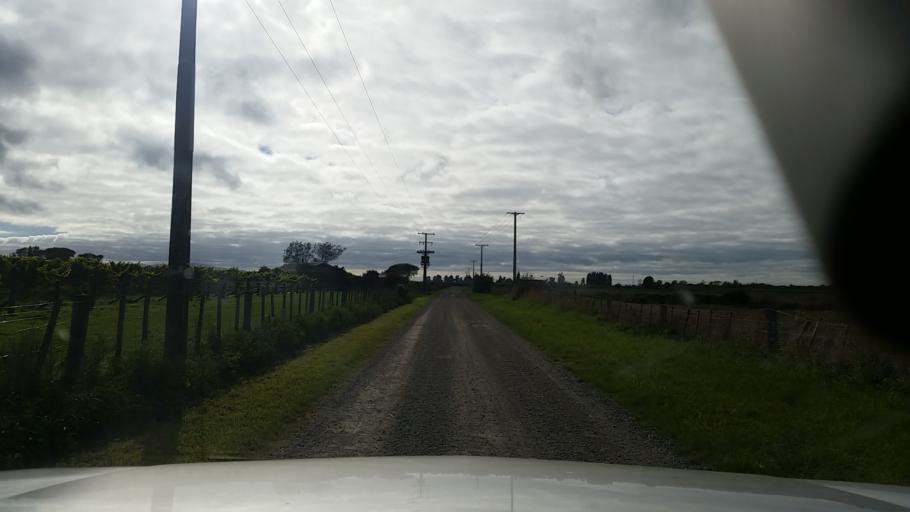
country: NZ
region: Marlborough
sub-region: Marlborough District
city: Blenheim
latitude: -41.4628
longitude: 173.9944
